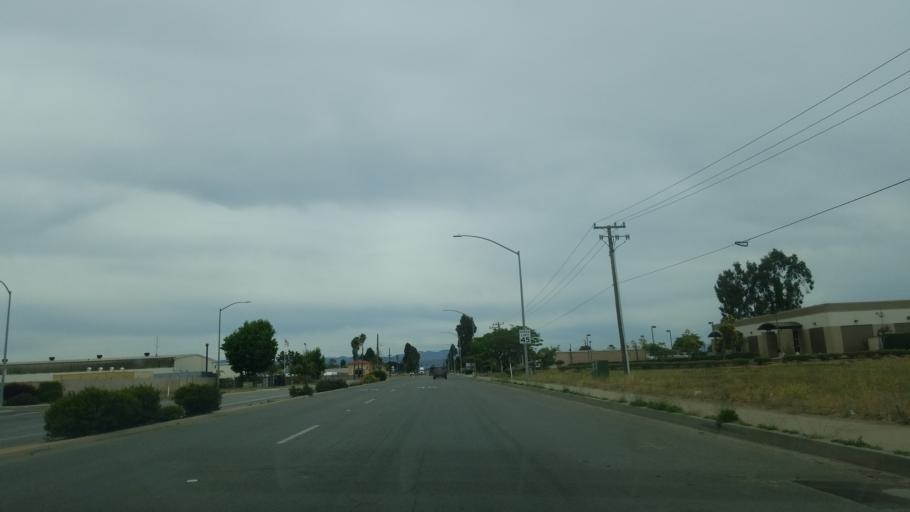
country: US
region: California
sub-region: Santa Barbara County
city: Santa Maria
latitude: 34.9207
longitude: -120.4607
